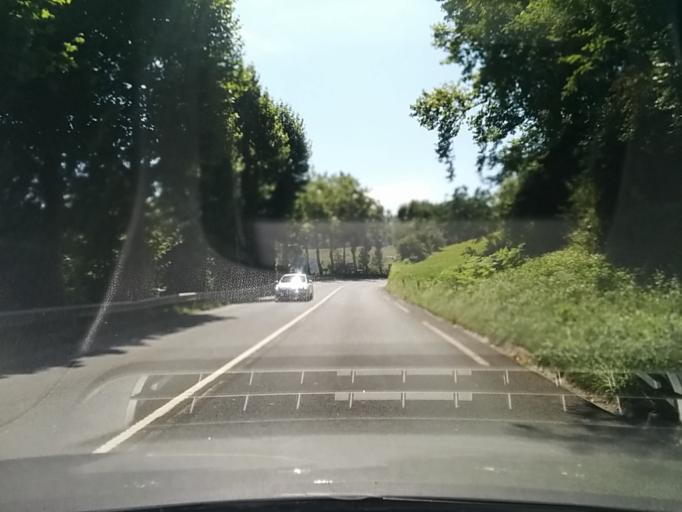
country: ES
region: Basque Country
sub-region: Provincia de Guipuzcoa
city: Zumaia
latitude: 43.2760
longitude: -2.2729
